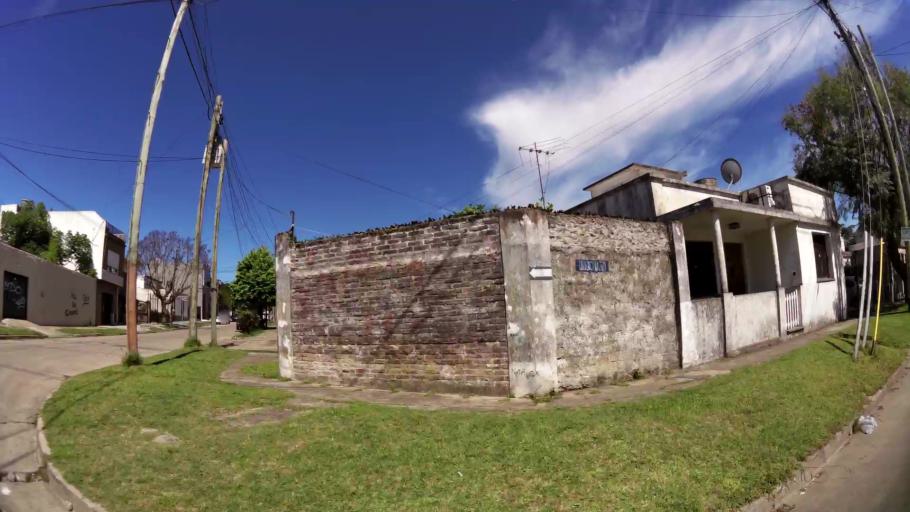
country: AR
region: Buenos Aires
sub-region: Partido de Quilmes
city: Quilmes
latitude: -34.7096
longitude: -58.2652
